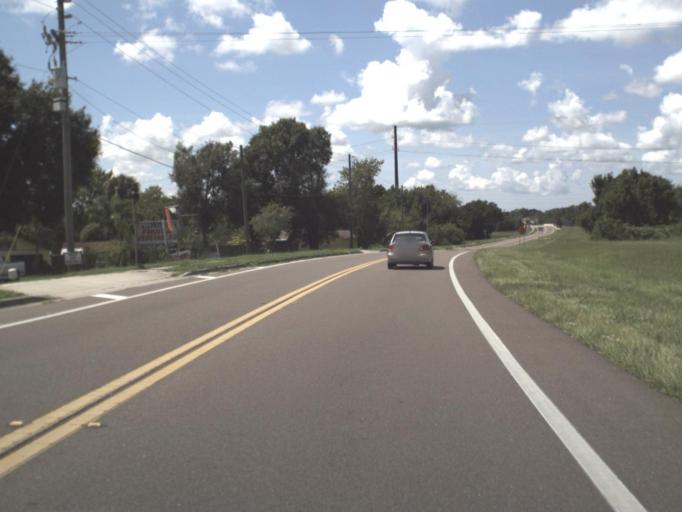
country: US
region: Florida
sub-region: DeSoto County
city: Nocatee
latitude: 27.1711
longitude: -81.8760
